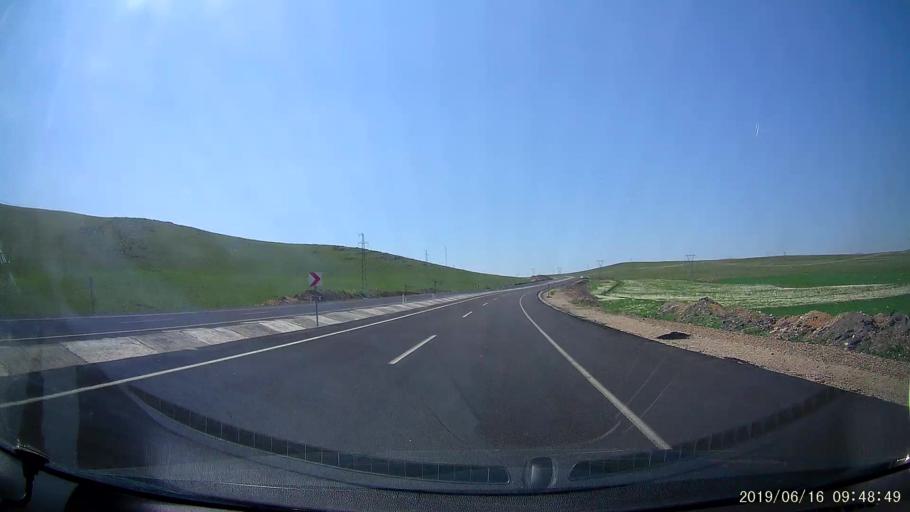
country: TR
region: Kars
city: Digor
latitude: 40.4292
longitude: 43.3559
